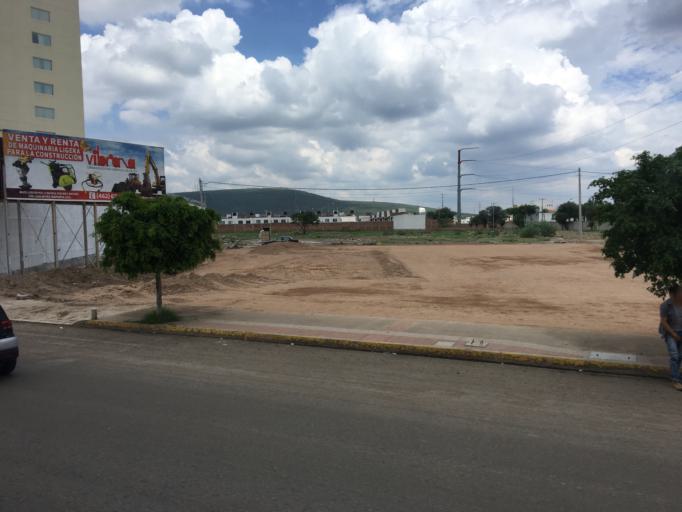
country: MX
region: Guanajuato
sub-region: Irapuato
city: Ex-Hacienda del Copal
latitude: 20.7161
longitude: -101.3493
